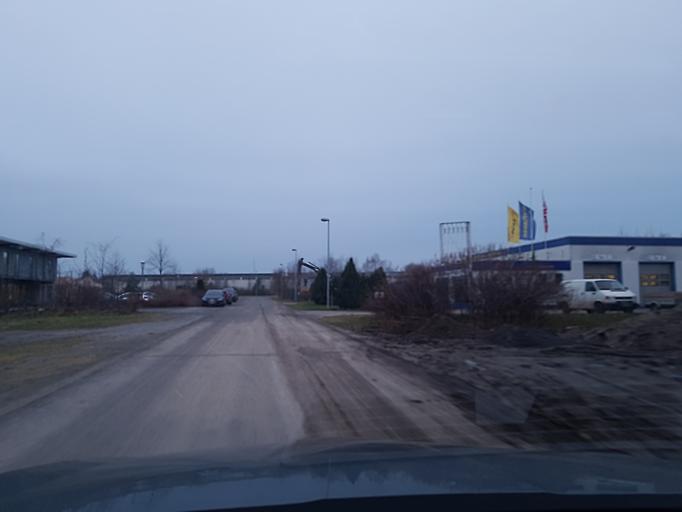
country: DE
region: Brandenburg
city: Doberlug-Kirchhain
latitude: 51.6294
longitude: 13.5854
